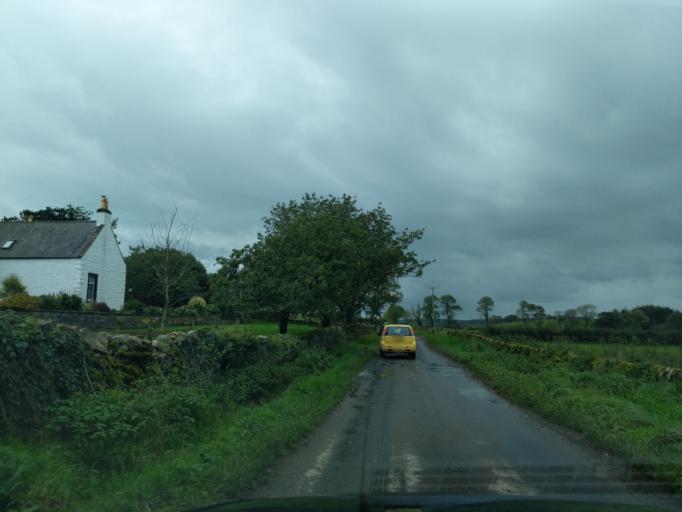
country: GB
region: Scotland
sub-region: Dumfries and Galloway
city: Castle Douglas
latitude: 54.9024
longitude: -3.9864
